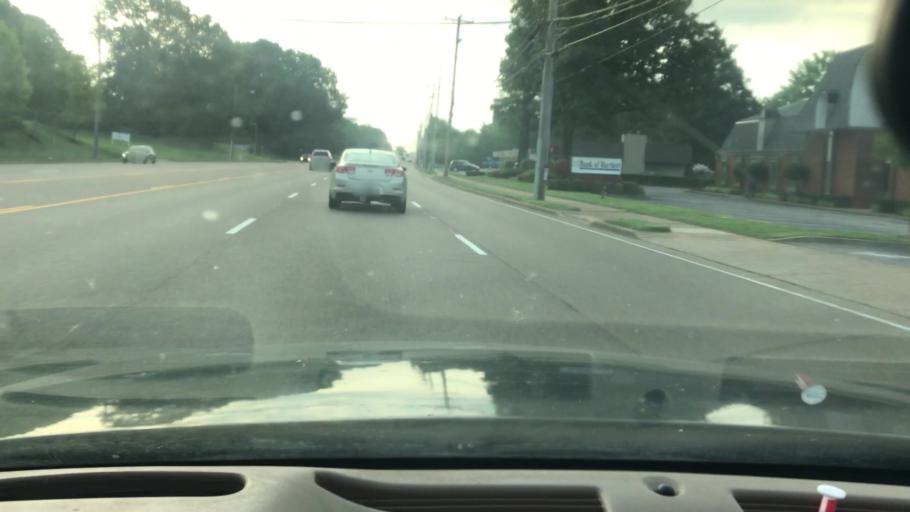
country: US
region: Tennessee
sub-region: Shelby County
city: Bartlett
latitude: 35.2047
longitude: -89.8545
